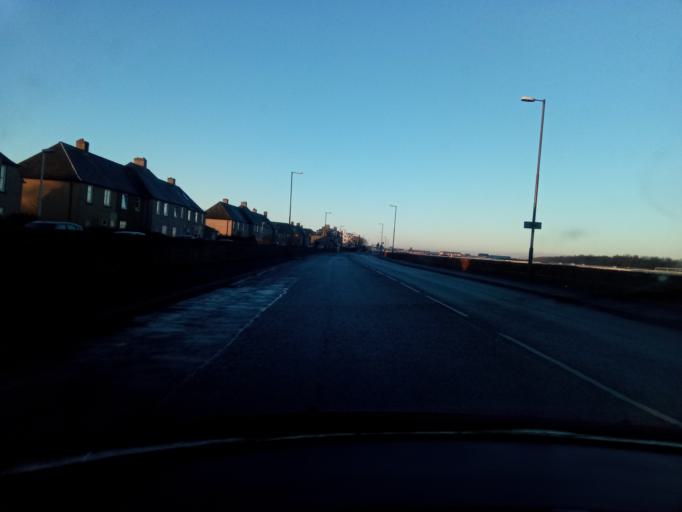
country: GB
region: Scotland
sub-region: East Lothian
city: Musselburgh
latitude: 55.9445
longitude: -3.0282
